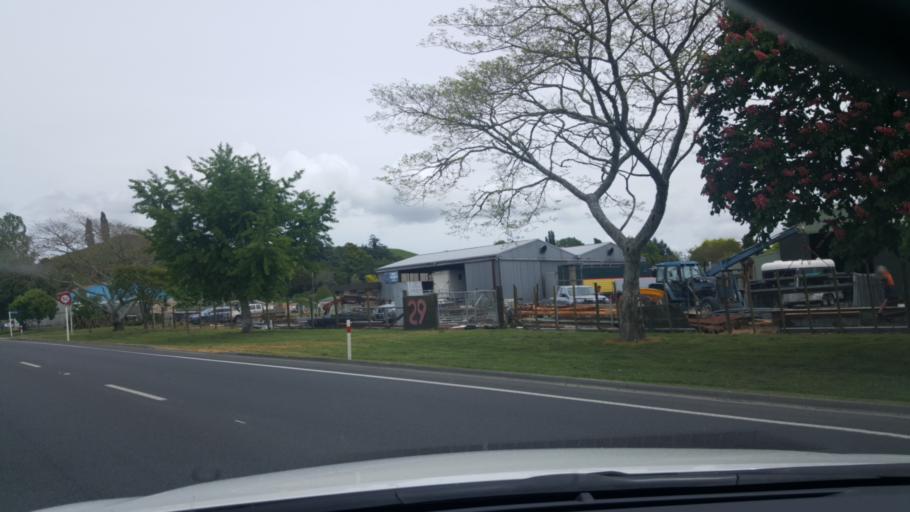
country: NZ
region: Waikato
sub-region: Matamata-Piako District
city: Matamata
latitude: -37.9722
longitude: 175.7543
